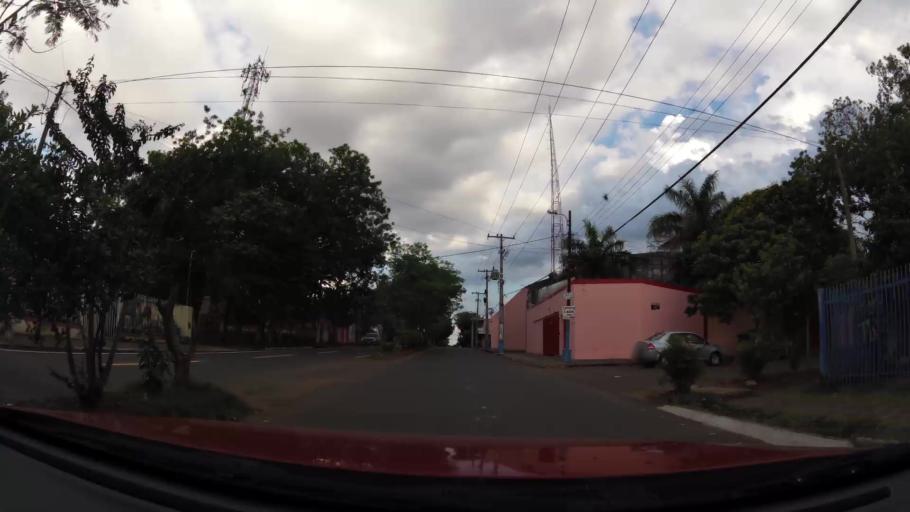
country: PY
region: Central
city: Villa Elisa
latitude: -25.3676
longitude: -57.5589
